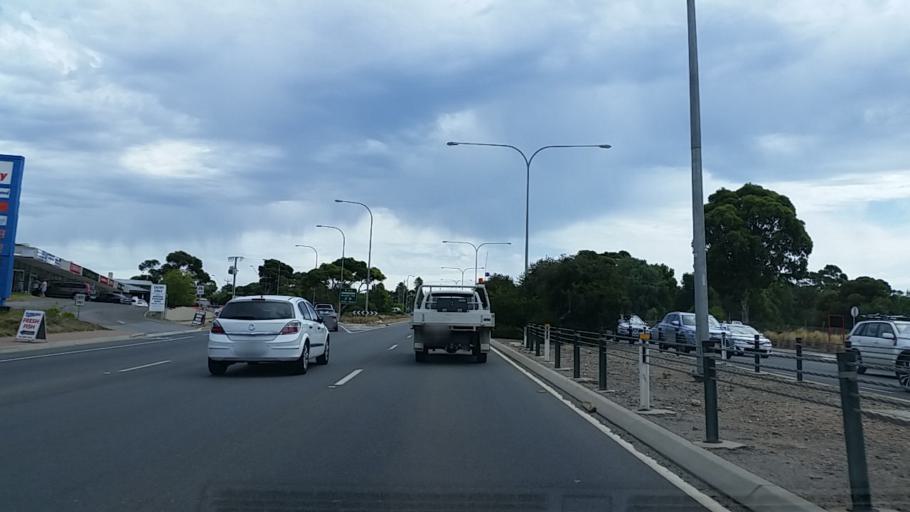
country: AU
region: South Australia
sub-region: Onkaparinga
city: Noarlunga
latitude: -35.1811
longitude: 138.4952
